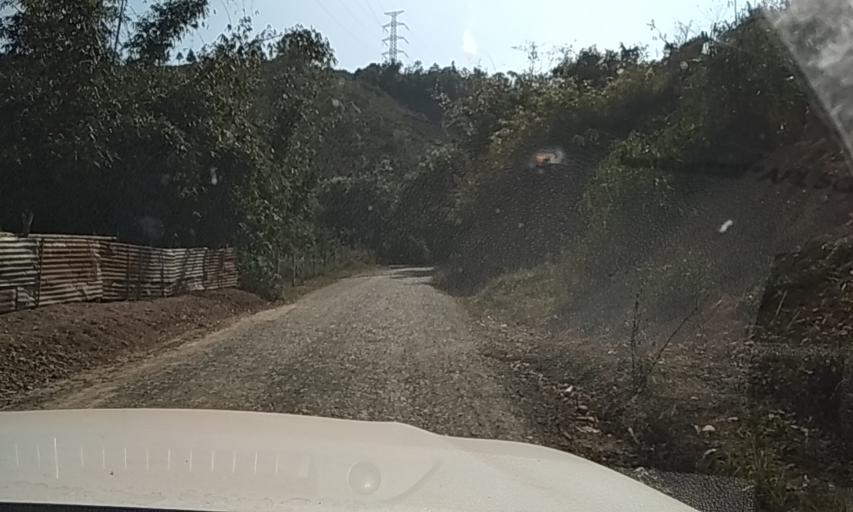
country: LA
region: Phongsali
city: Phongsali
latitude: 21.6577
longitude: 102.0904
